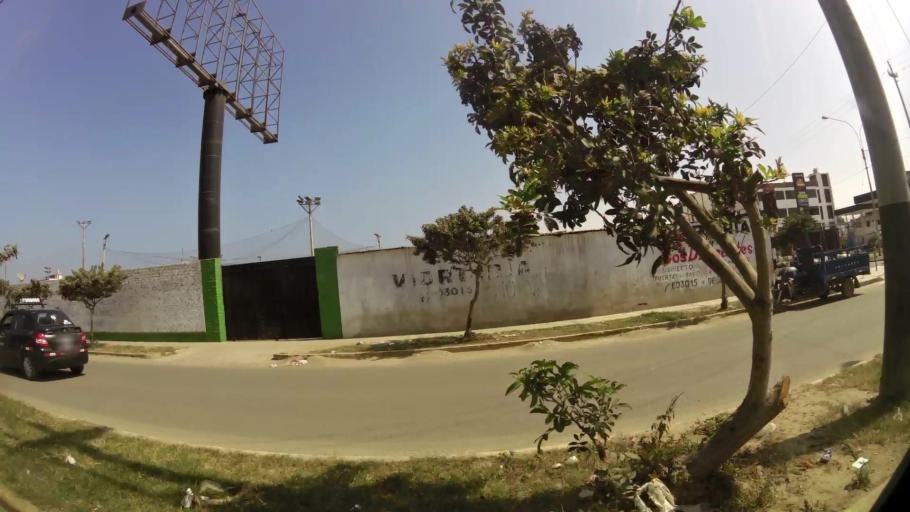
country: PE
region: La Libertad
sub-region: Provincia de Trujillo
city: Buenos Aires
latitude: -8.1241
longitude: -79.0441
